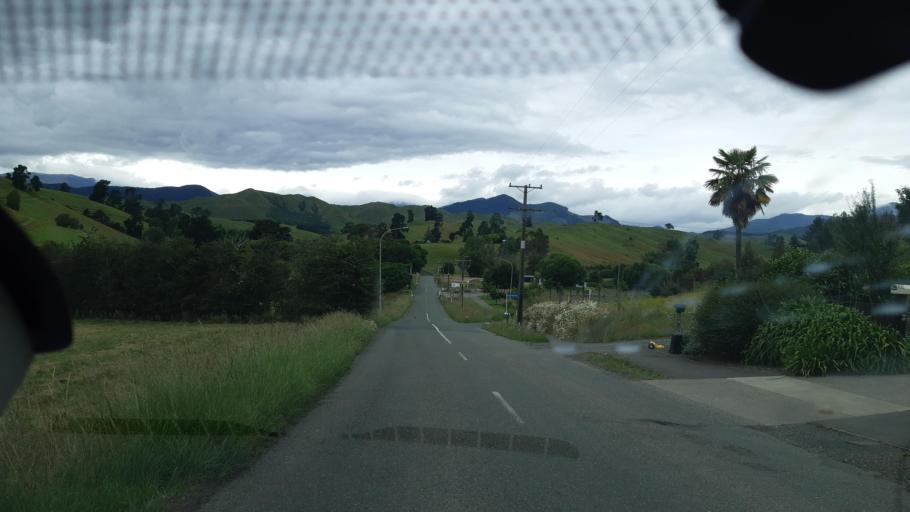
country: NZ
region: Tasman
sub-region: Tasman District
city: Wakefield
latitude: -41.4112
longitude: 173.0491
